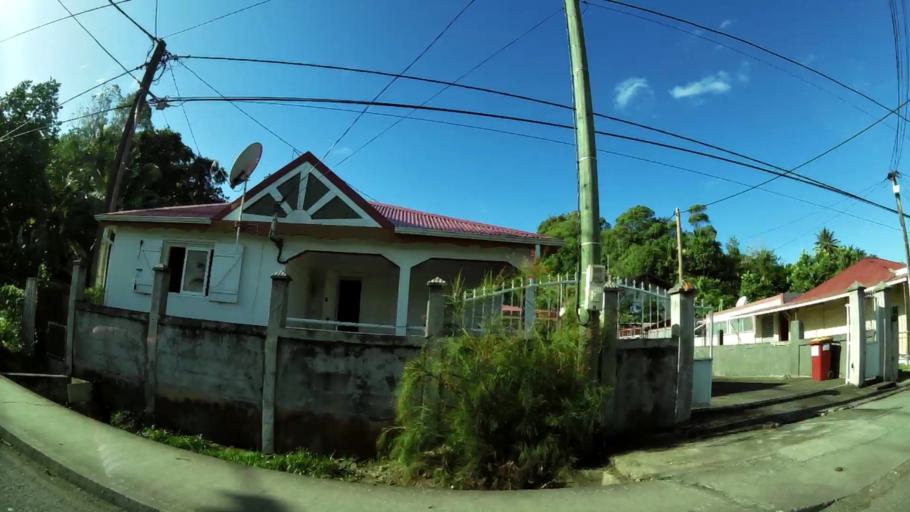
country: GP
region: Guadeloupe
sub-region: Guadeloupe
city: Petit-Canal
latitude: 16.3259
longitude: -61.4467
